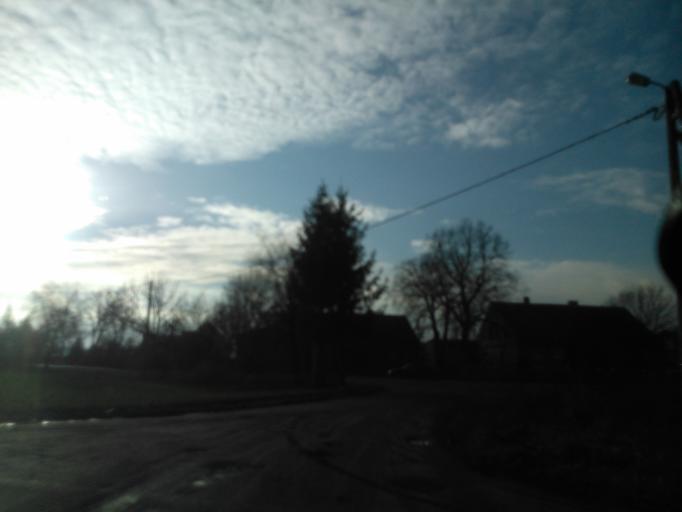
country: PL
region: Kujawsko-Pomorskie
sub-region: Powiat wabrzeski
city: Debowa Laka
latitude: 53.2169
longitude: 19.1200
